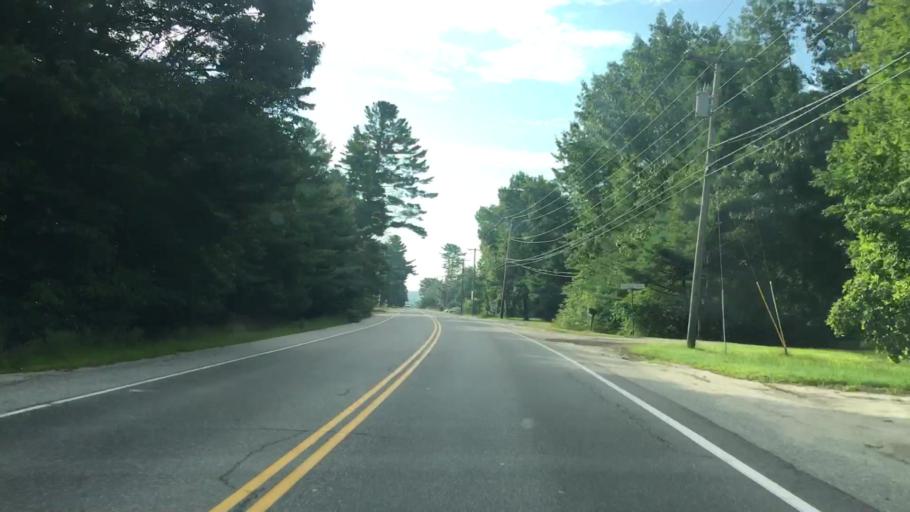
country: US
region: Maine
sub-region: Cumberland County
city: North Windham
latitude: 43.8166
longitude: -70.4304
